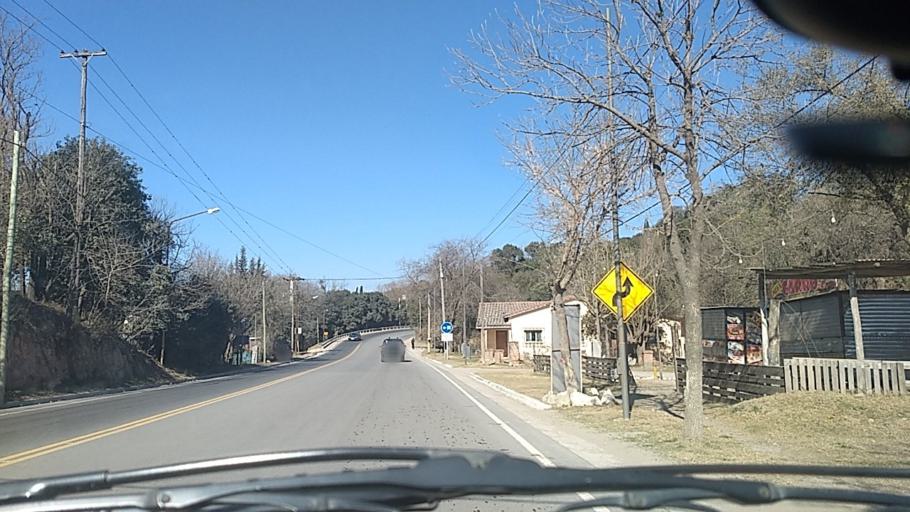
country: AR
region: Cordoba
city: Salsipuedes
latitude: -31.1082
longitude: -64.2916
